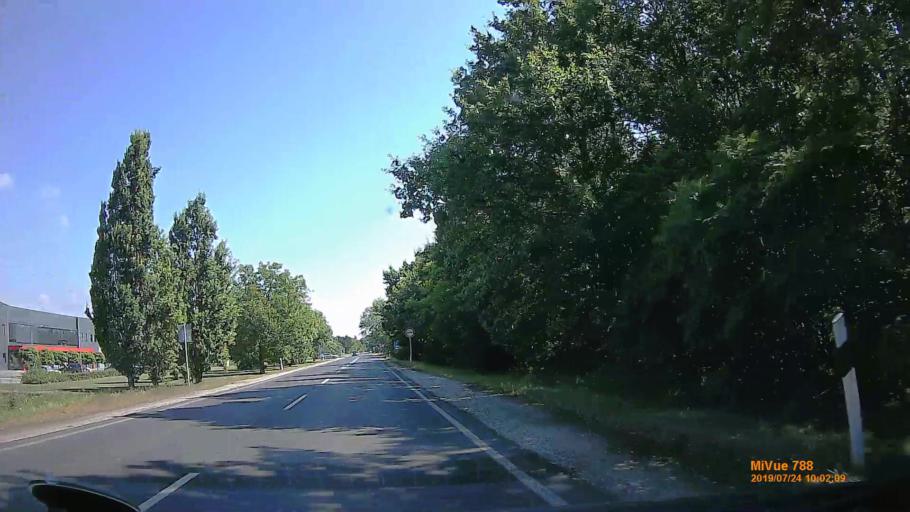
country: HU
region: Szabolcs-Szatmar-Bereg
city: Vasarosnameny
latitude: 48.1084
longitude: 22.3038
